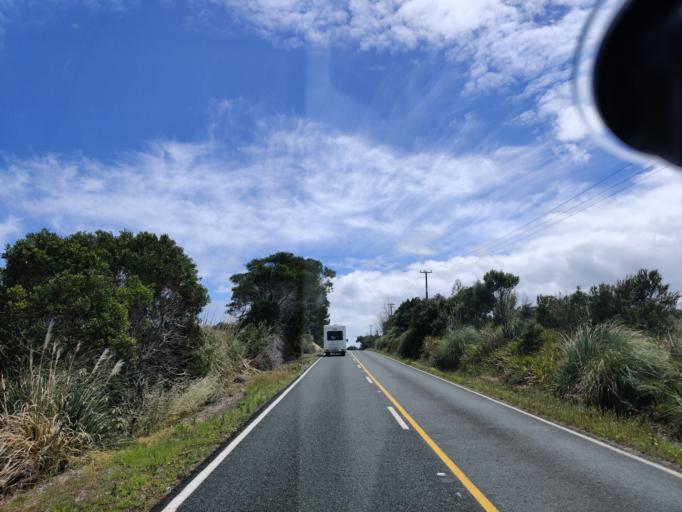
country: NZ
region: Northland
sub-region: Far North District
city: Kaitaia
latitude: -34.7555
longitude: 173.0639
